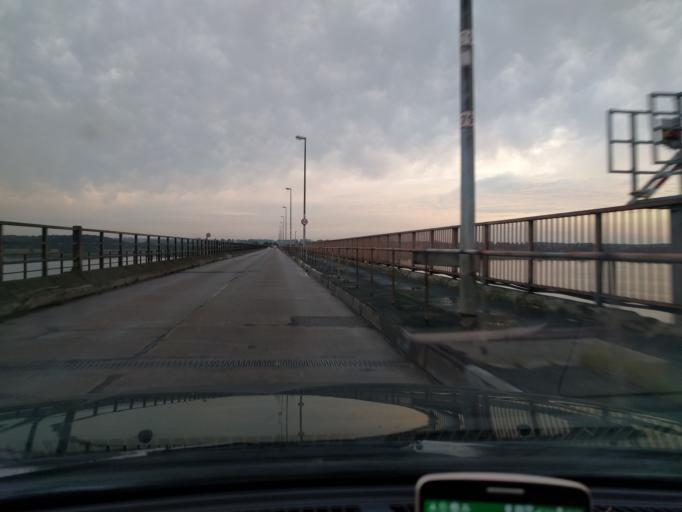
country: DK
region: Zealand
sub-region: Guldborgsund Kommune
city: Norre Alslev
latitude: 54.9560
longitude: 11.8735
